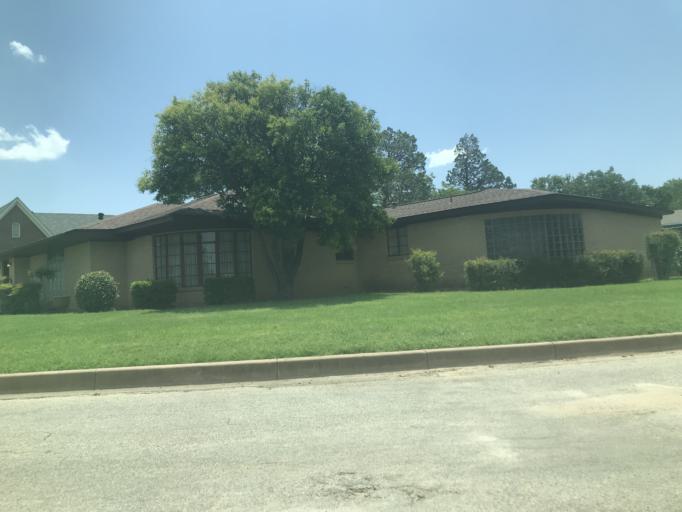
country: US
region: Texas
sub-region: Taylor County
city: Abilene
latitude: 32.4671
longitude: -99.7158
